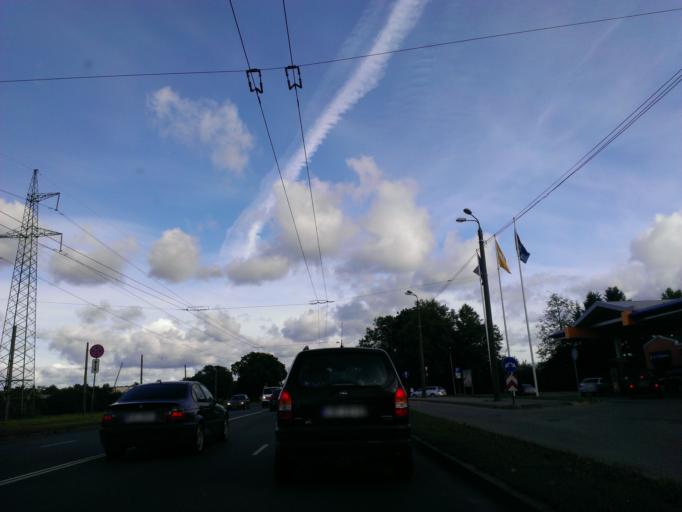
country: LV
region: Stopini
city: Ulbroka
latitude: 56.9588
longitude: 24.2332
